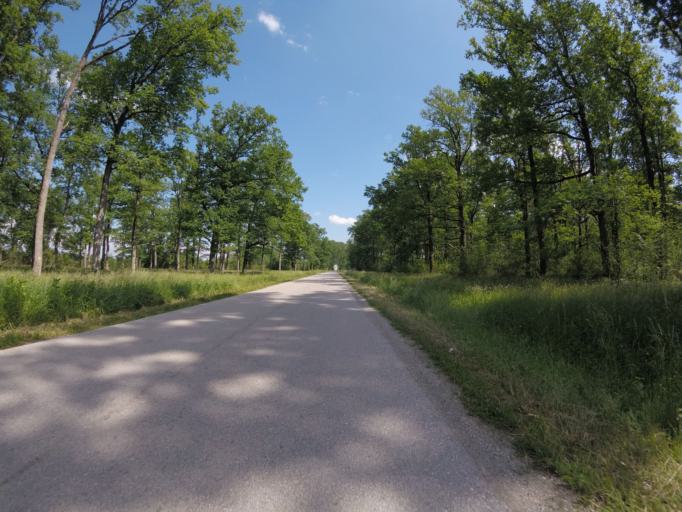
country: HR
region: Zagrebacka
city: Kuce
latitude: 45.6745
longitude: 16.1710
